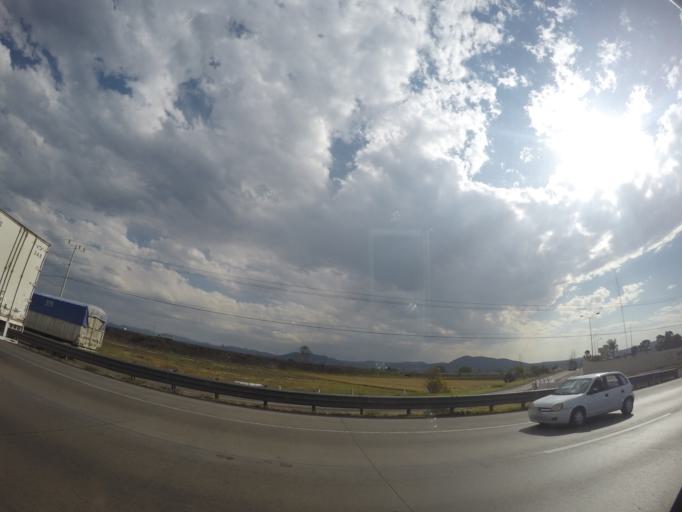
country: MX
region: Queretaro
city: Pedro Escobedo
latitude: 20.4948
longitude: -100.1301
